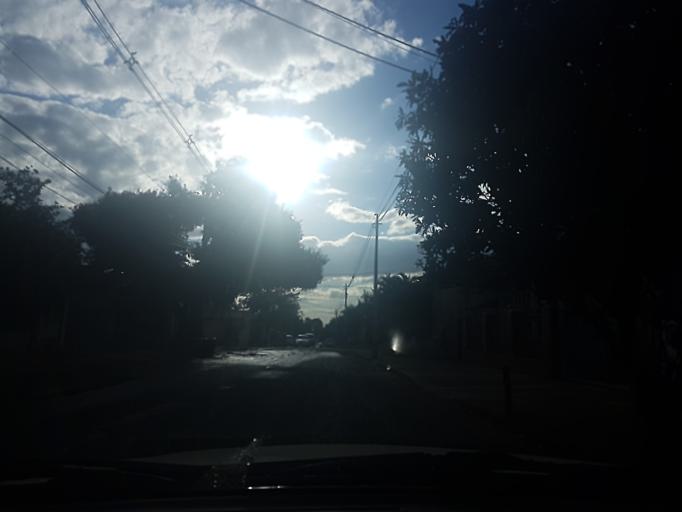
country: PY
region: Asuncion
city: Asuncion
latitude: -25.2700
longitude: -57.5776
